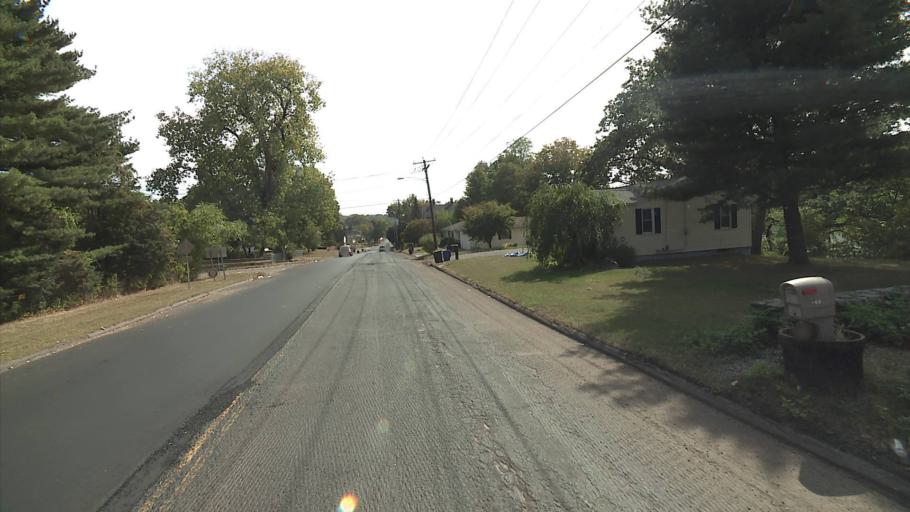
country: US
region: Connecticut
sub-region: Fairfield County
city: Shelton
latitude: 41.3307
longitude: -73.1098
